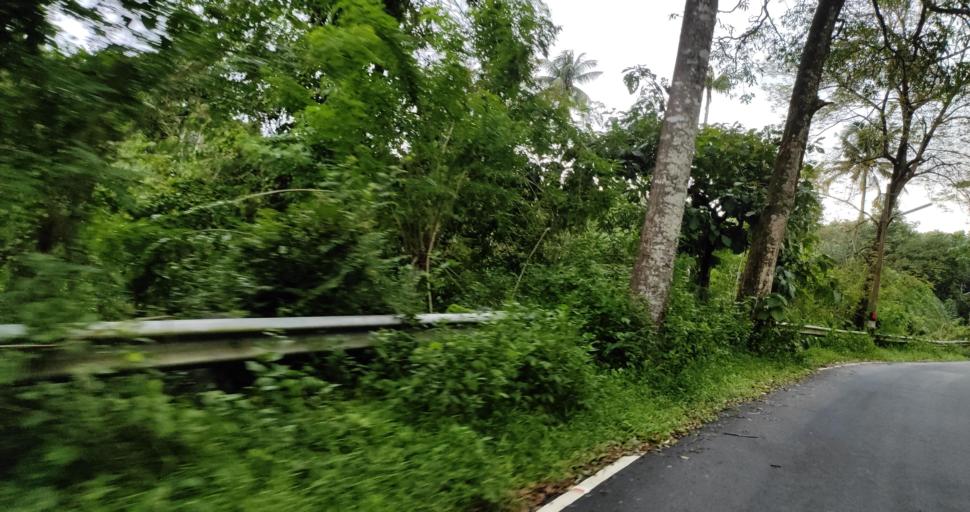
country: IN
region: Kerala
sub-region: Thrissur District
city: Kizhake Chalakudi
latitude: 10.3009
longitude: 76.4454
